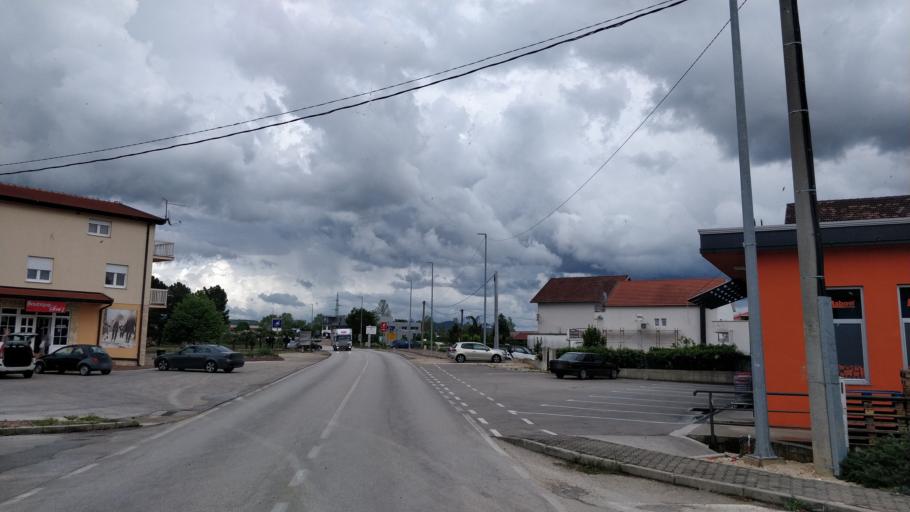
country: BA
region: Federation of Bosnia and Herzegovina
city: Ljubuski
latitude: 43.1878
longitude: 17.5395
